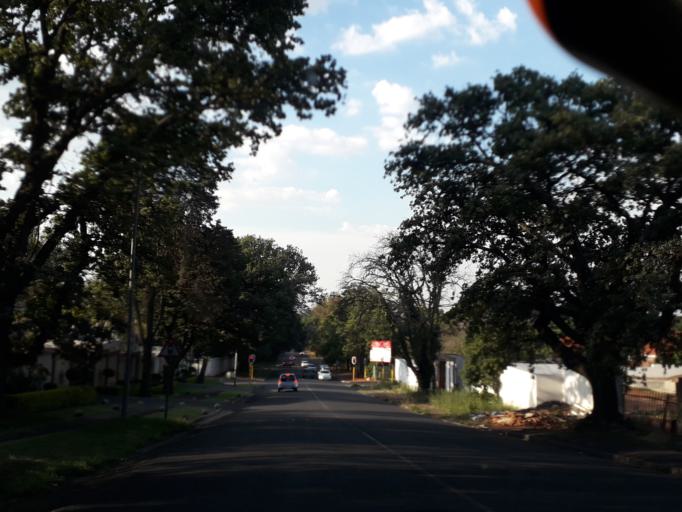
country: ZA
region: Gauteng
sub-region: City of Johannesburg Metropolitan Municipality
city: Johannesburg
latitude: -26.1698
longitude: 28.0650
